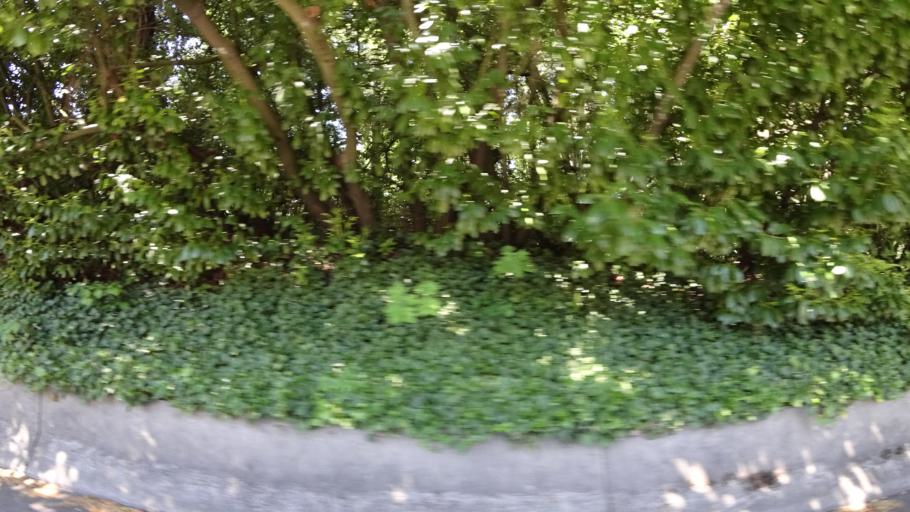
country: US
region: Oregon
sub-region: Multnomah County
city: Portland
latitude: 45.4799
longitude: -122.6906
